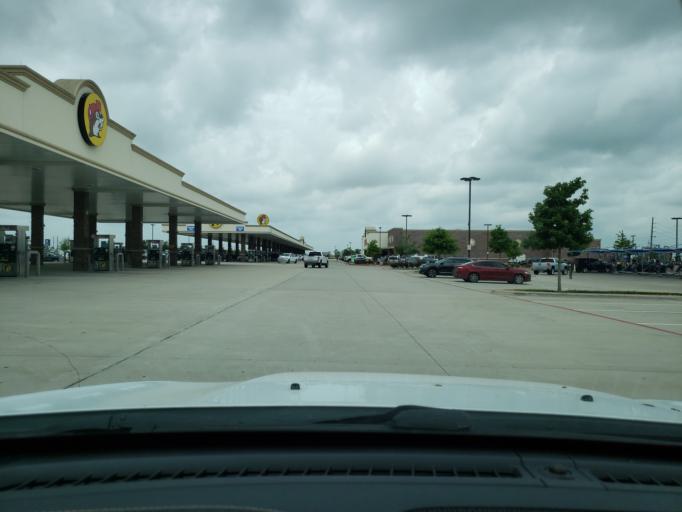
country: US
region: Texas
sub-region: Harris County
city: Katy
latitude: 29.7783
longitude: -95.8457
